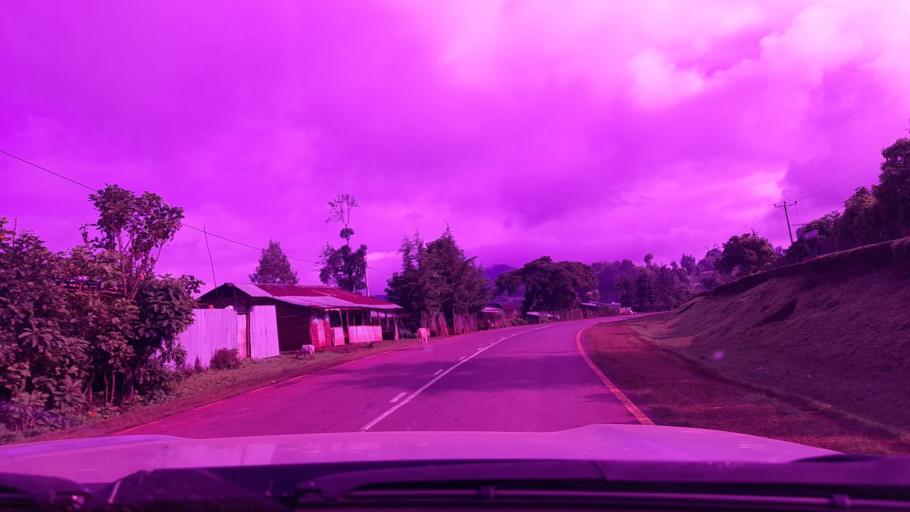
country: ET
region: Oromiya
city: Bedele
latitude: 8.2229
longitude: 36.4473
